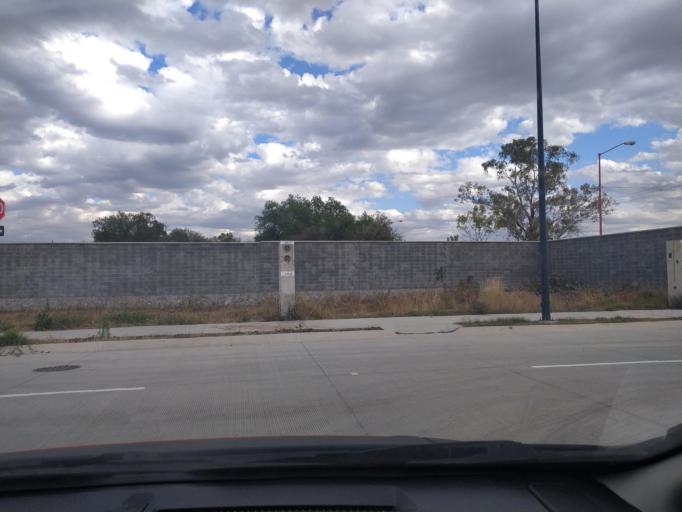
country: LA
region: Oudomxai
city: Muang La
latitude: 21.0228
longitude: 101.8229
